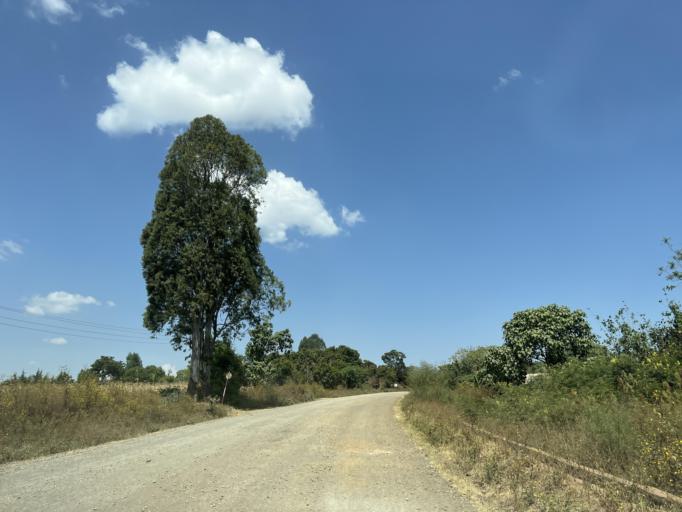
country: ET
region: Oromiya
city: Shambu
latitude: 9.2672
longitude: 36.5175
